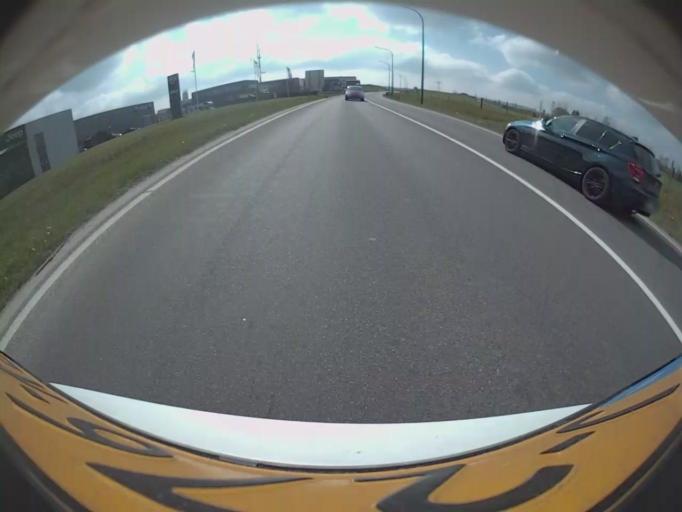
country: BE
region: Wallonia
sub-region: Province du Luxembourg
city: Marche-en-Famenne
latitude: 50.2409
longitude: 5.3378
